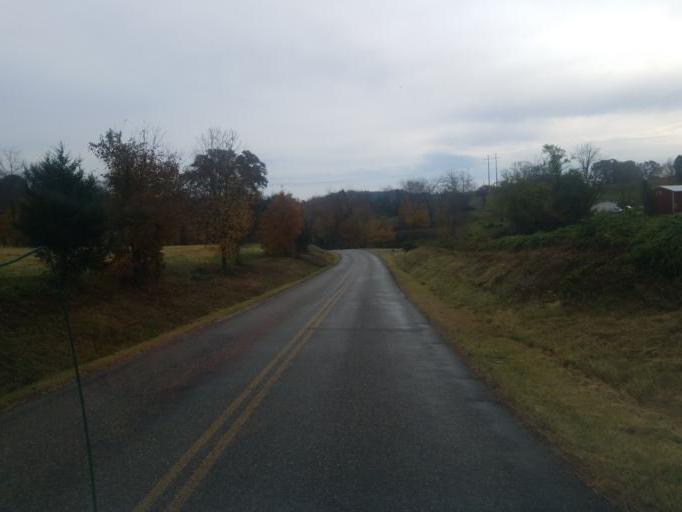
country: US
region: Ohio
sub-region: Washington County
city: Beverly
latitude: 39.5524
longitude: -81.6755
